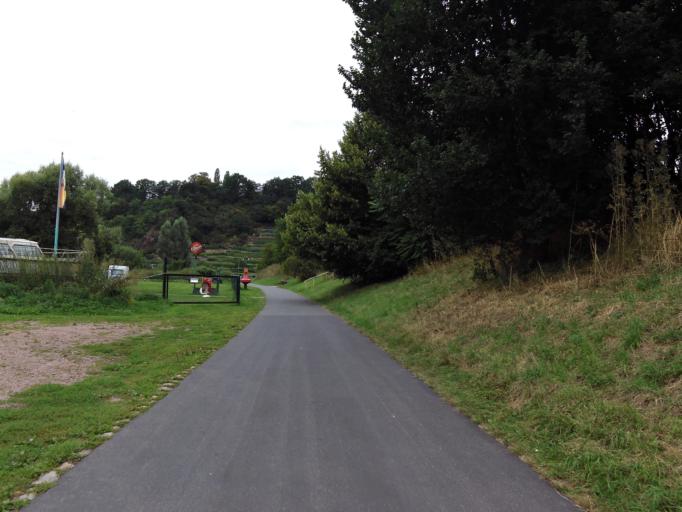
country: DE
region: Saxony
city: Meissen
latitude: 51.1717
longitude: 13.4755
